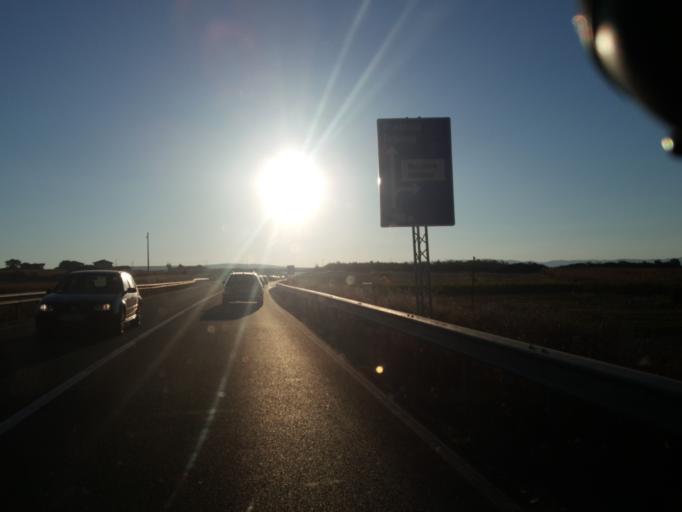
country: XK
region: Prizren
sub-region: Komuna e Malisheves
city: Llazice
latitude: 42.5758
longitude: 20.7167
